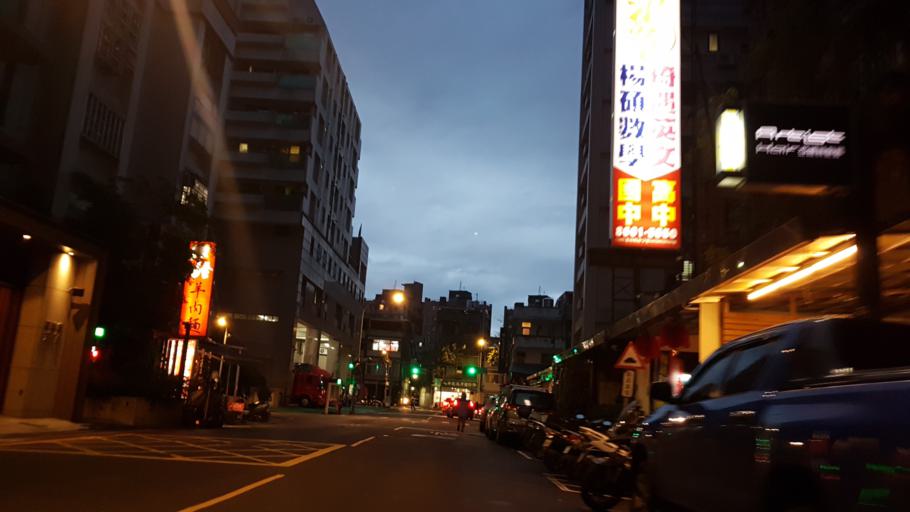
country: TW
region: Taipei
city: Taipei
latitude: 24.9793
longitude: 121.5552
